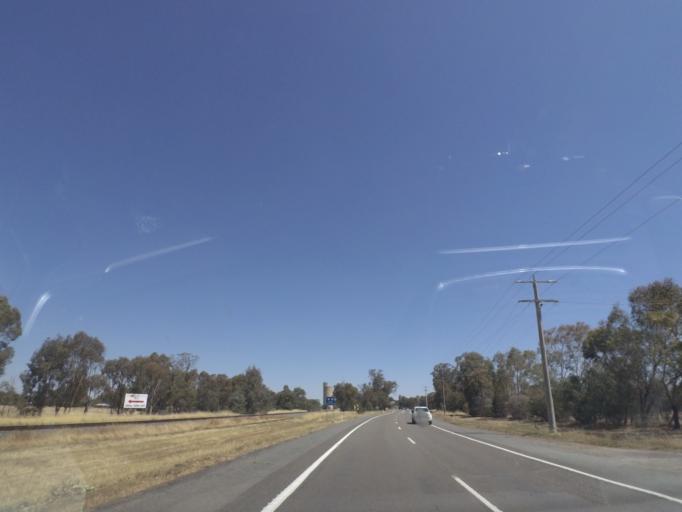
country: AU
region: Victoria
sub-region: Greater Shepparton
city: Shepparton
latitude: -36.2337
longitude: 145.4318
